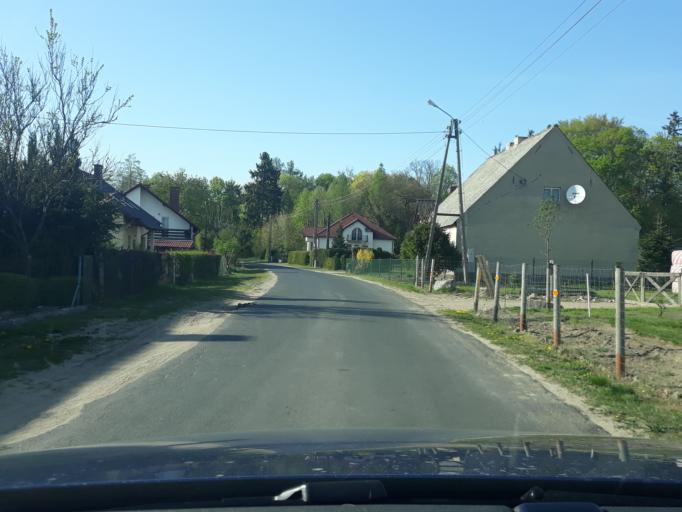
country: PL
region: Pomeranian Voivodeship
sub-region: Powiat czluchowski
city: Przechlewo
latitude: 53.8731
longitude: 17.3318
